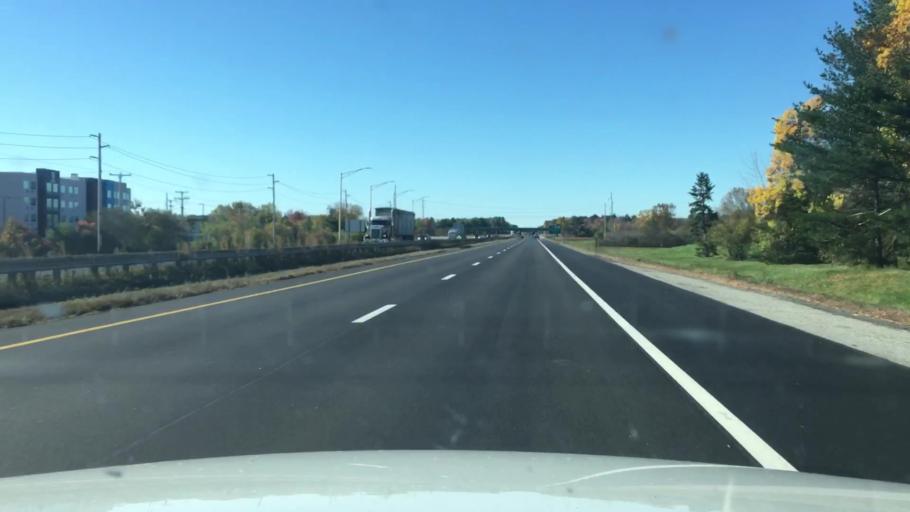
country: US
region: Maine
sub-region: Cumberland County
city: South Portland Gardens
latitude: 43.6369
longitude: -70.3394
